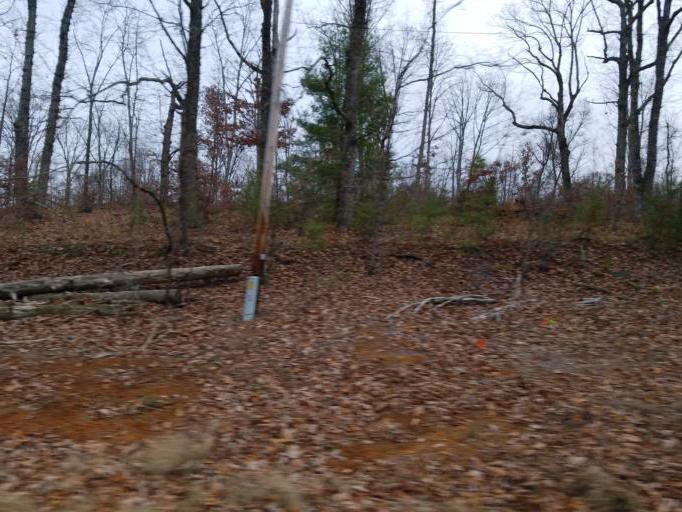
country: US
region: Georgia
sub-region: Dawson County
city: Dawsonville
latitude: 34.4320
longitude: -84.0618
